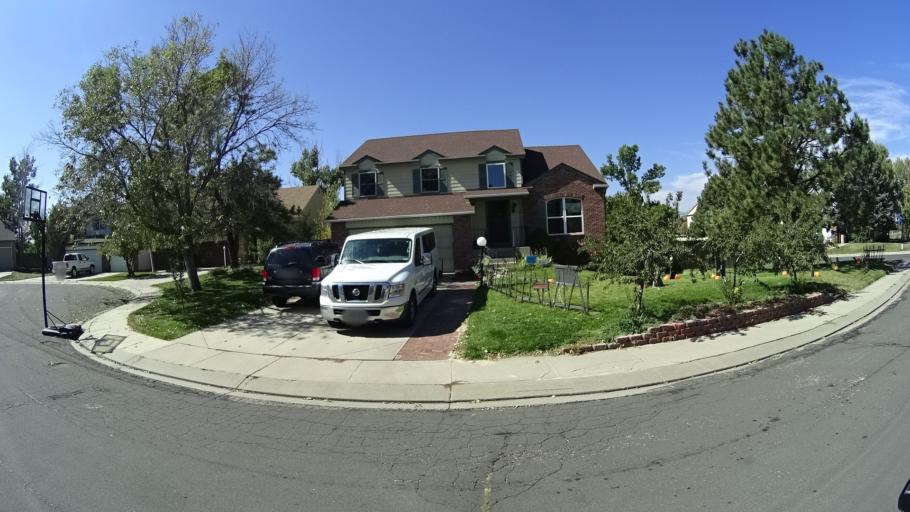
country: US
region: Colorado
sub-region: El Paso County
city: Cimarron Hills
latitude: 38.8985
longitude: -104.7033
